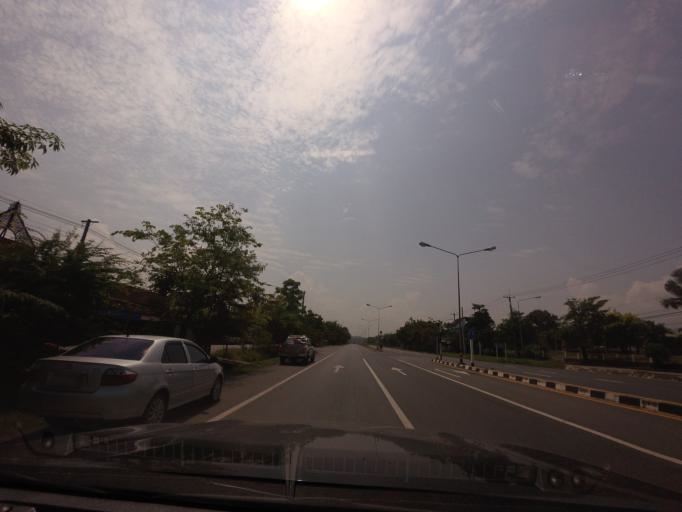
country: TH
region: Phrae
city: Den Chai
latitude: 17.9649
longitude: 100.0664
